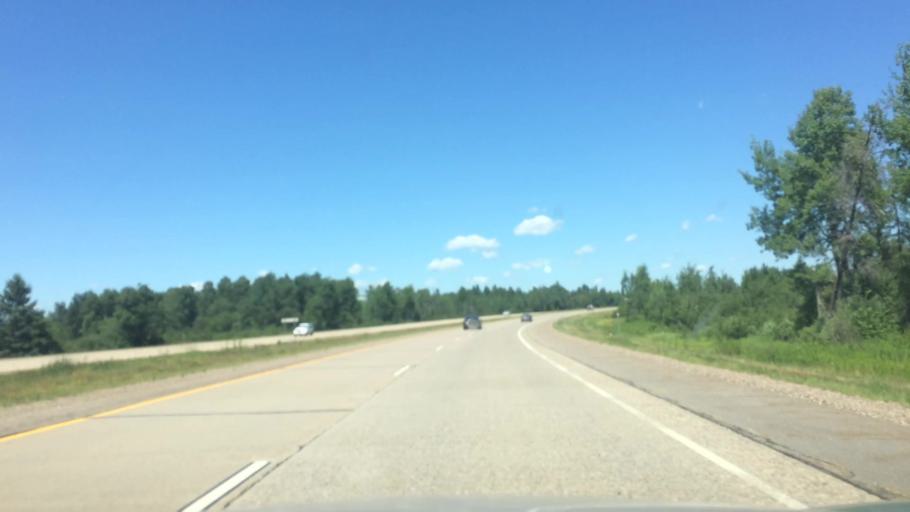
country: US
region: Wisconsin
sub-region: Lincoln County
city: Tomahawk
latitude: 45.3818
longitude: -89.6715
